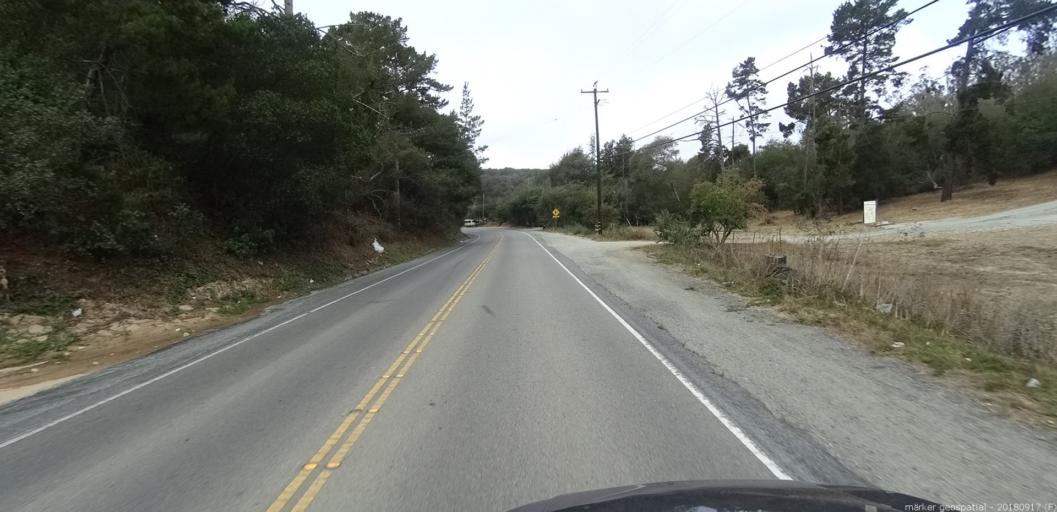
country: US
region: California
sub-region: Monterey County
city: Prunedale
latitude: 36.8001
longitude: -121.6950
